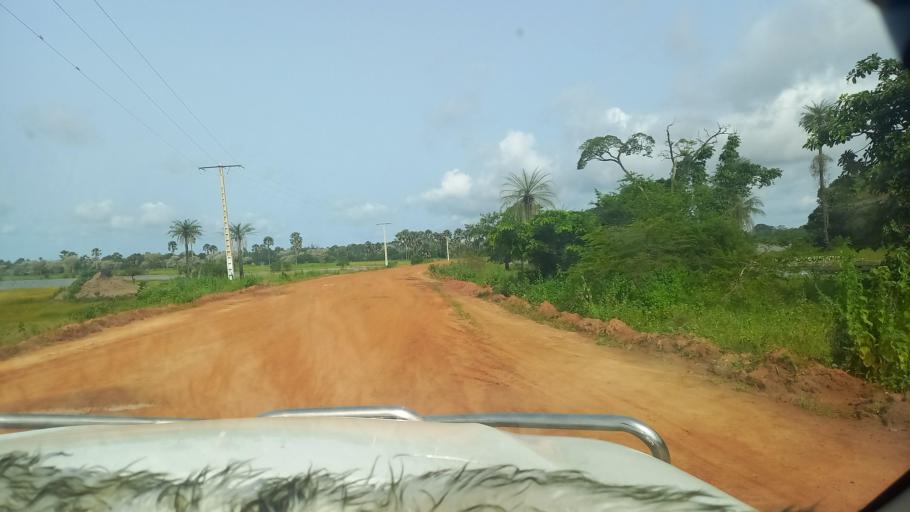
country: SN
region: Ziguinchor
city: Ziguinchor
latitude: 12.6714
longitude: -16.2789
